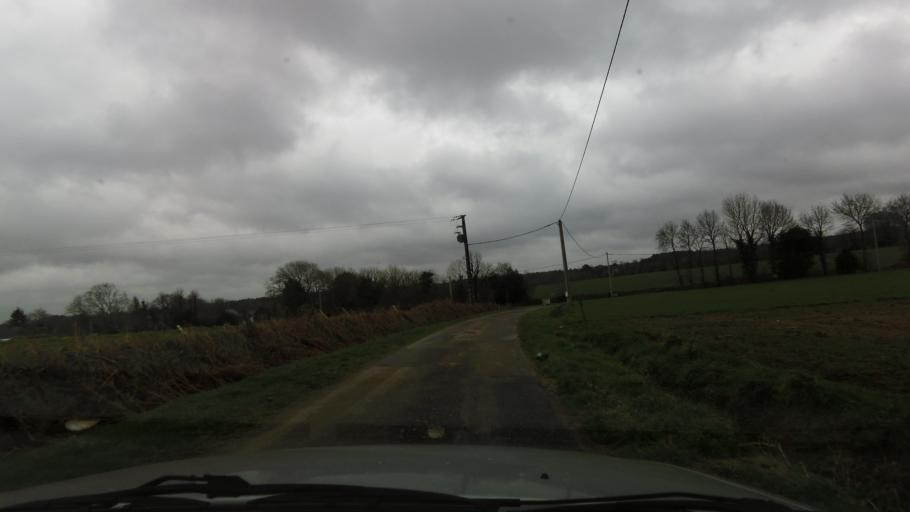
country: FR
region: Brittany
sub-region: Departement du Morbihan
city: Molac
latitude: 47.7698
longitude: -2.4633
